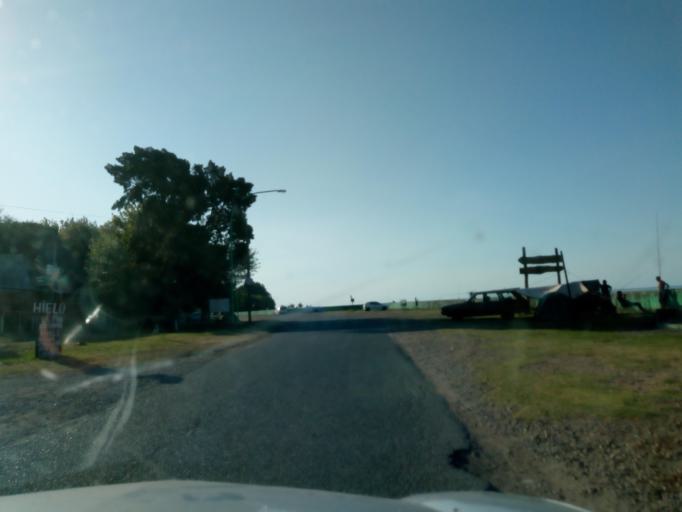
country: AR
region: Buenos Aires
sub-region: Partido de Ensenada
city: Ensenada
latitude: -34.7921
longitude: -57.9962
